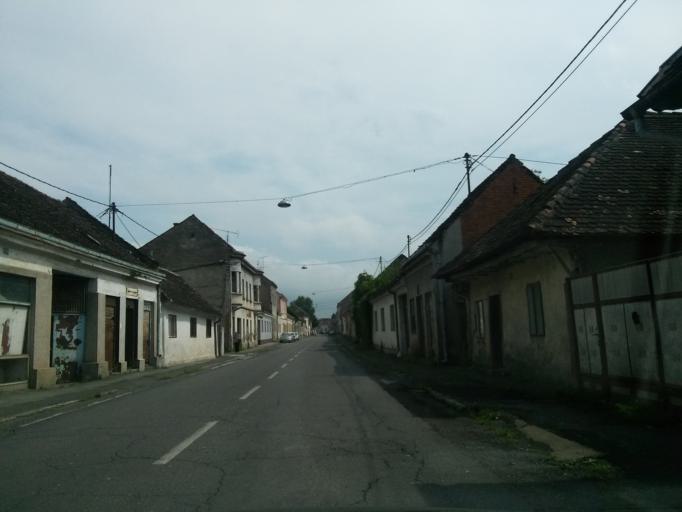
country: HR
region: Sisacko-Moslavacka
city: Glina
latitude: 45.3357
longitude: 16.0863
